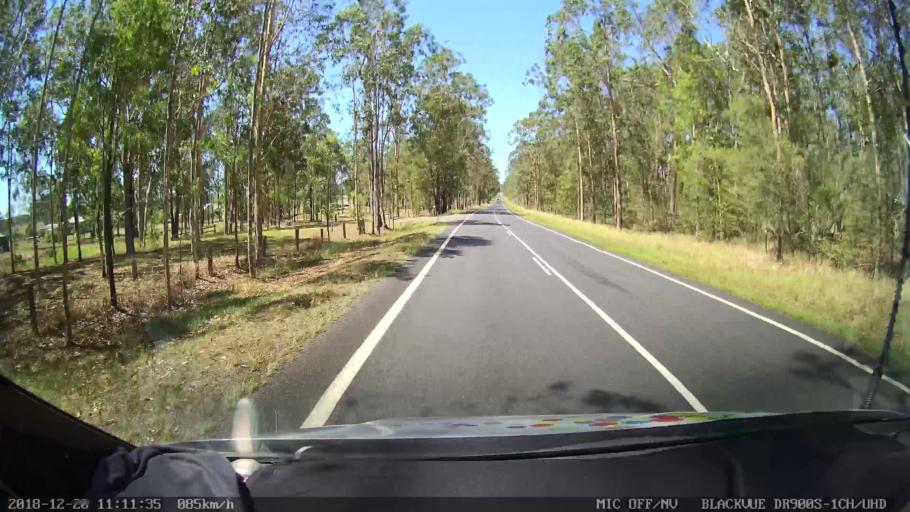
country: AU
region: New South Wales
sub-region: Richmond Valley
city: Casino
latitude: -28.9628
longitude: 153.0133
